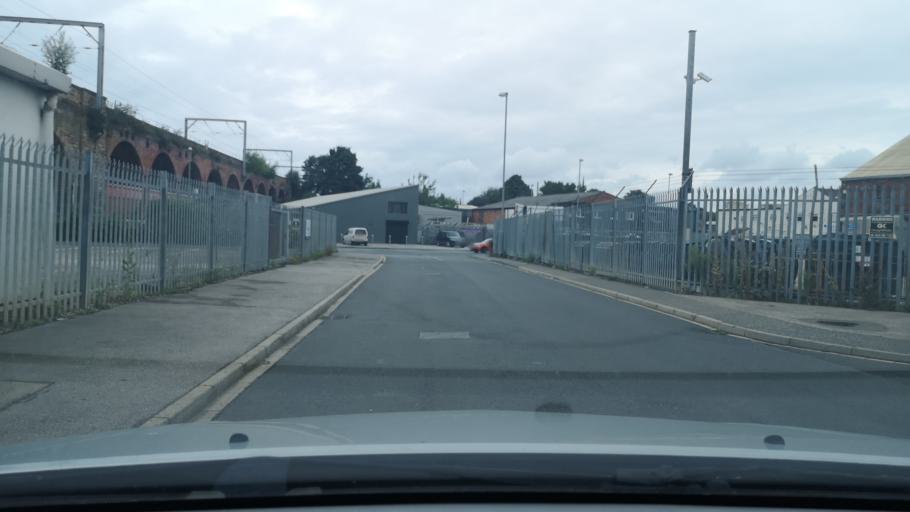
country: GB
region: England
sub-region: City and Borough of Wakefield
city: Wakefield
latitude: 53.6735
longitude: -1.4965
